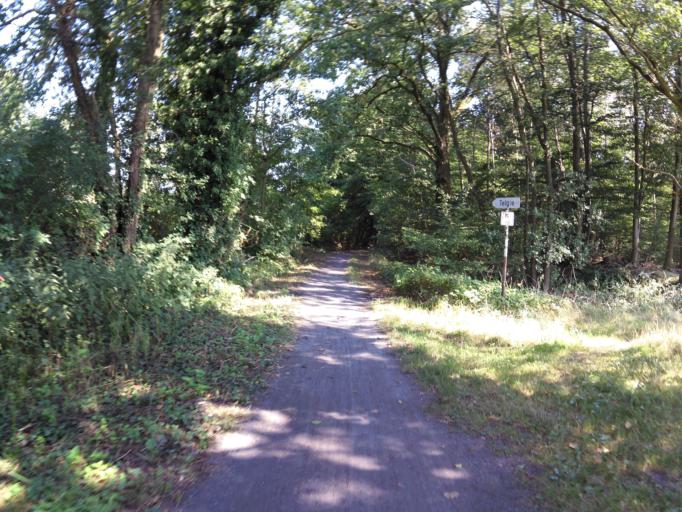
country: DE
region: North Rhine-Westphalia
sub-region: Regierungsbezirk Munster
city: Telgte
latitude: 51.9606
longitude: 7.7295
